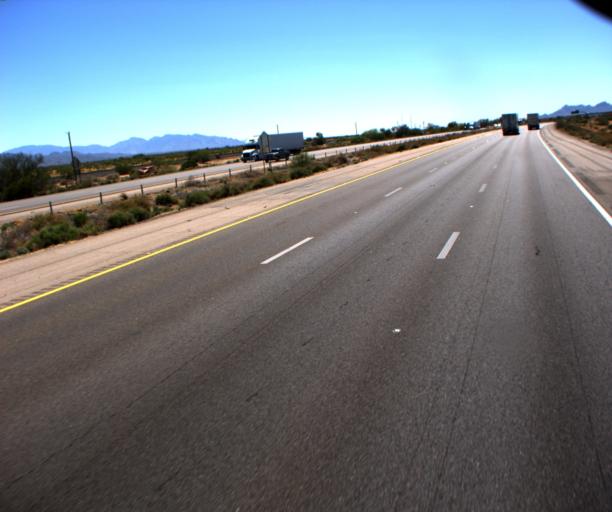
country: US
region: Arizona
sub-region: Pima County
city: Avra Valley
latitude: 32.5151
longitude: -111.2745
